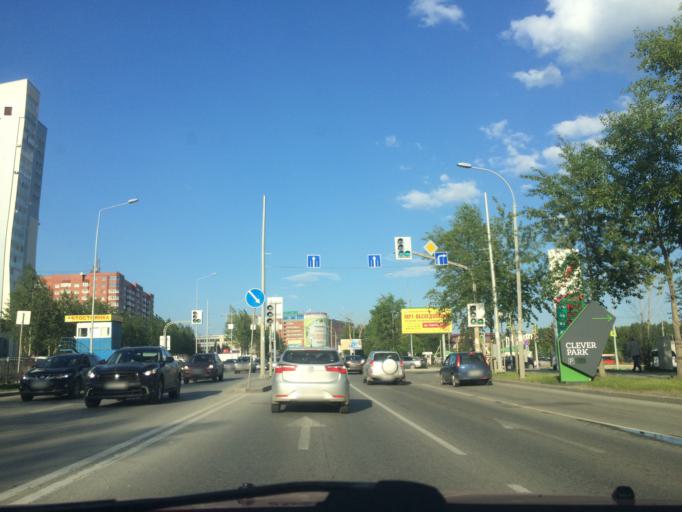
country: RU
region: Sverdlovsk
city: Yekaterinburg
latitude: 56.8178
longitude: 60.6339
